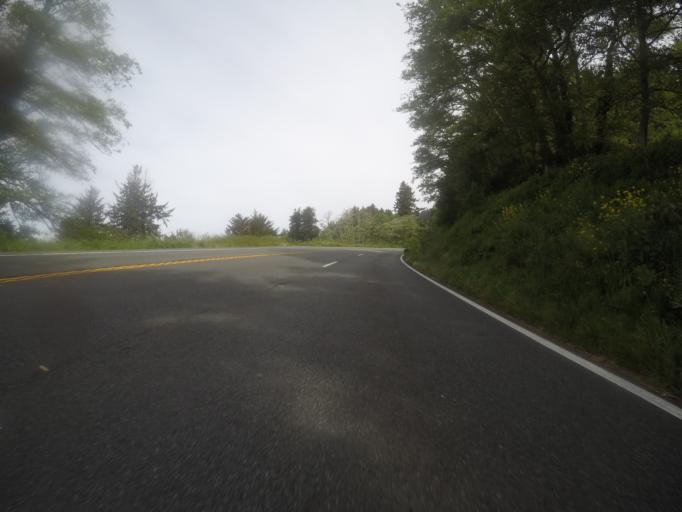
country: US
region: California
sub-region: Del Norte County
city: Bertsch-Oceanview
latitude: 41.6179
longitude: -124.1093
